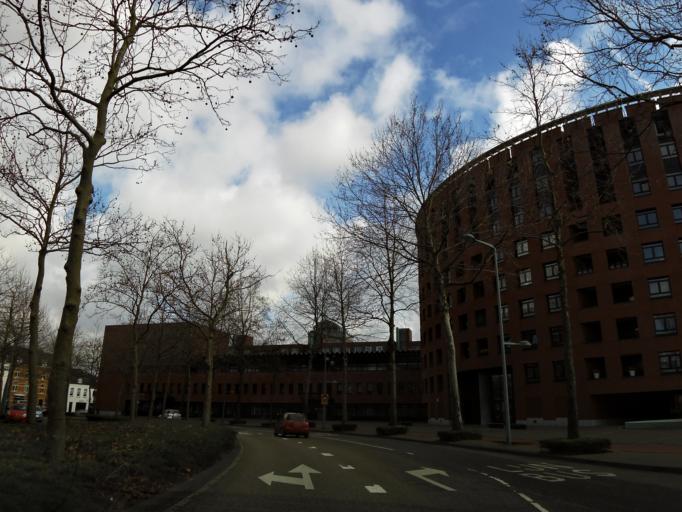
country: NL
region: Limburg
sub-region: Gemeente Maastricht
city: Maastricht
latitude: 50.8462
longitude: 5.7024
